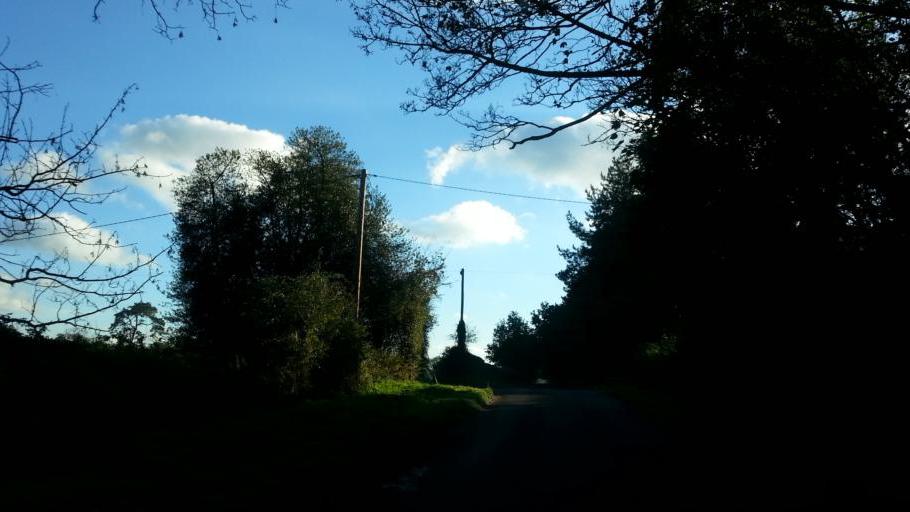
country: GB
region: England
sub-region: Suffolk
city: Thurston
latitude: 52.2444
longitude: 0.8065
